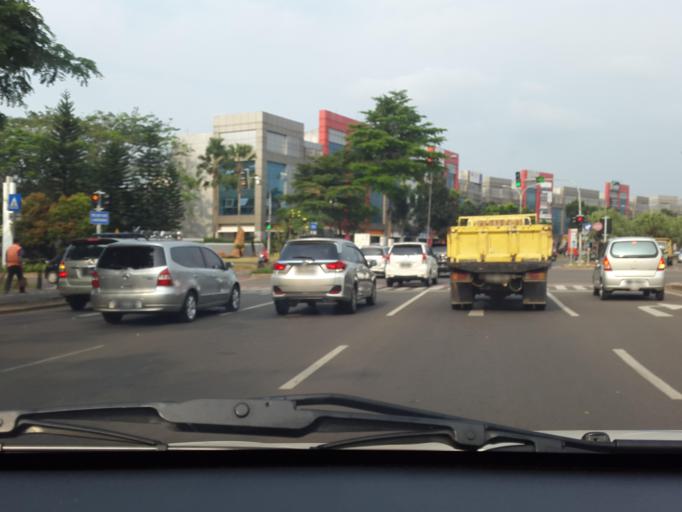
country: ID
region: Banten
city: South Tangerang
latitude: -6.2723
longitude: 106.7135
